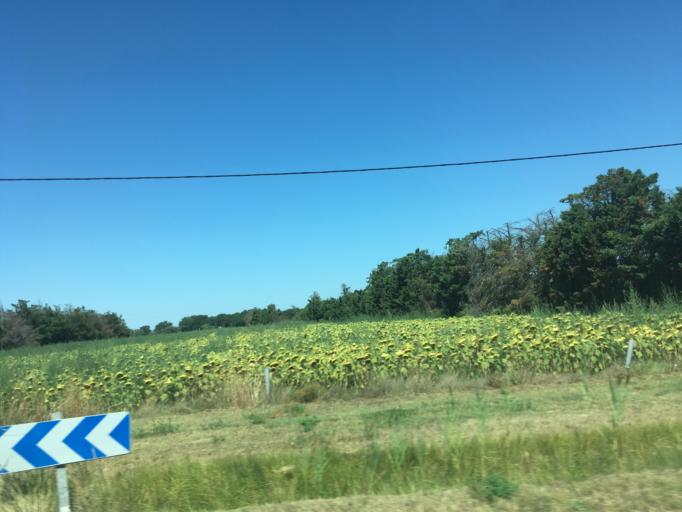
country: FR
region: Languedoc-Roussillon
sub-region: Departement du Gard
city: Fourques
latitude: 43.6574
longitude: 4.5804
